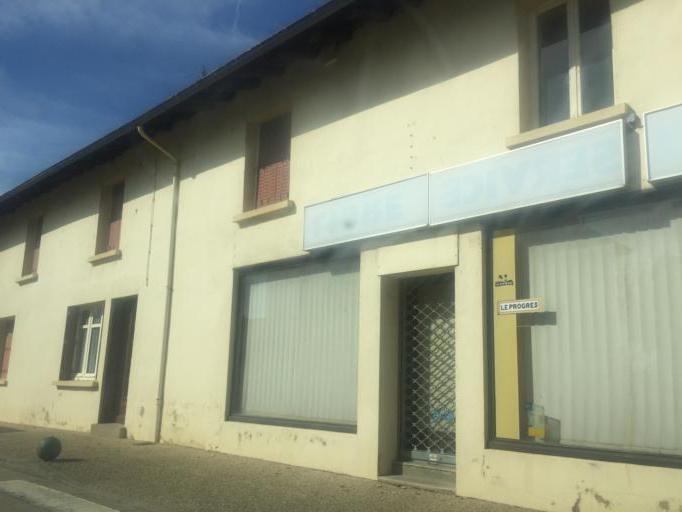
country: FR
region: Rhone-Alpes
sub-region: Departement de l'Ain
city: Marboz
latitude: 46.4106
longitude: 5.2649
